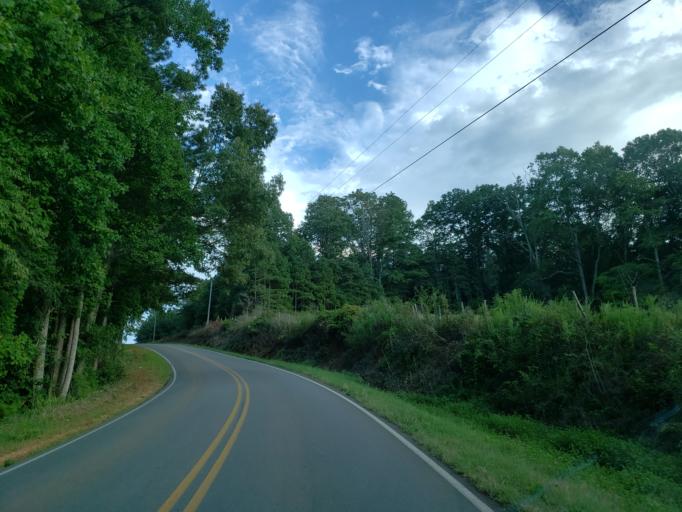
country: US
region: Georgia
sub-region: Cherokee County
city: Ball Ground
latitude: 34.3317
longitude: -84.4376
